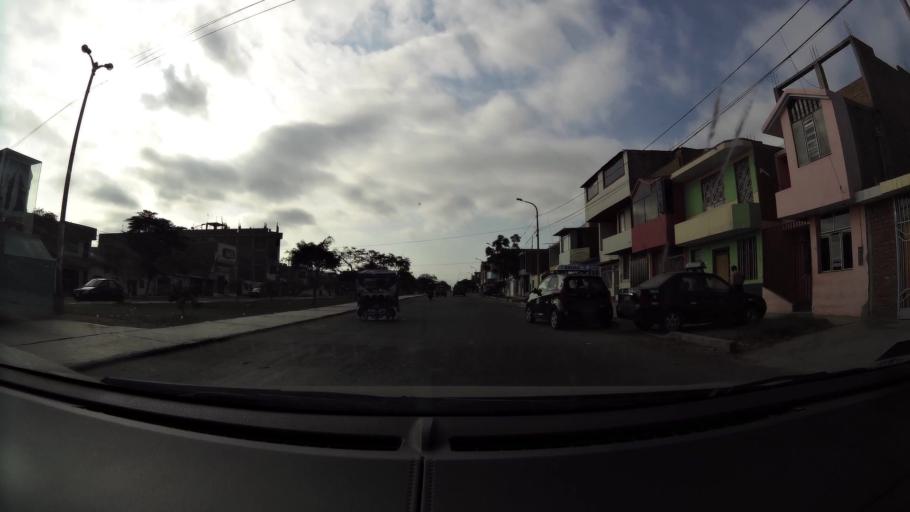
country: PE
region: La Libertad
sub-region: Provincia de Trujillo
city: La Esperanza
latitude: -8.0825
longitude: -79.0416
